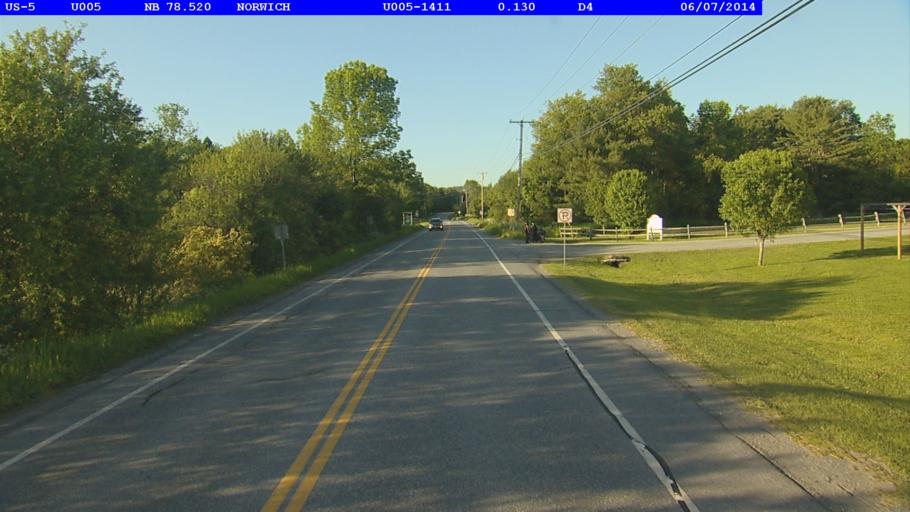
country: US
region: Vermont
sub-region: Windsor County
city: Wilder
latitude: 43.6979
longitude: -72.3177
